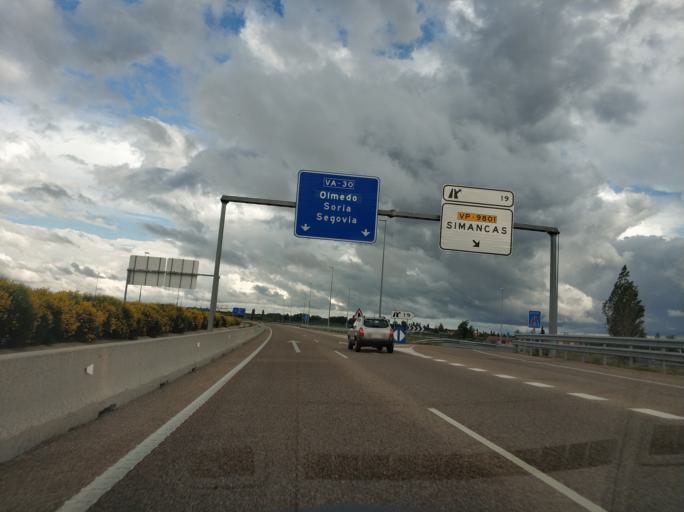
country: ES
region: Castille and Leon
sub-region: Provincia de Valladolid
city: Arroyo
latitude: 41.6128
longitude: -4.7726
